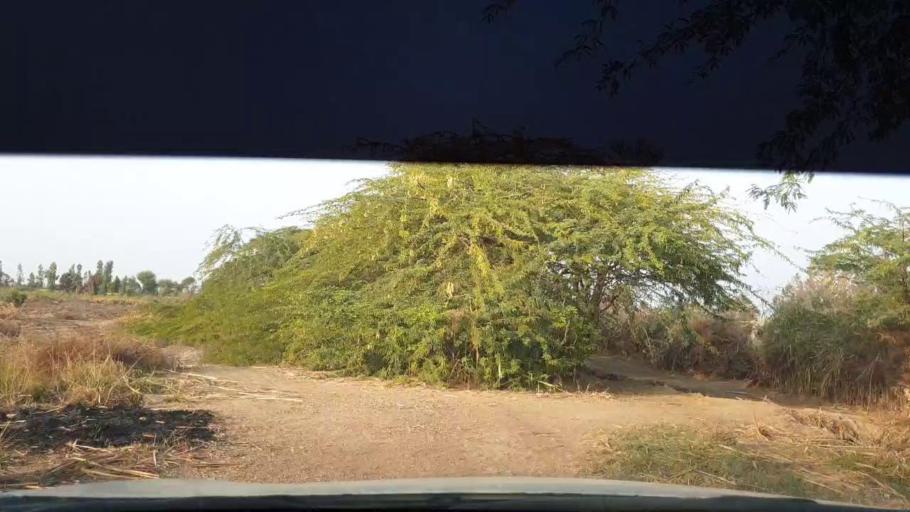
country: PK
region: Sindh
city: Berani
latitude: 25.7249
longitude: 68.9779
